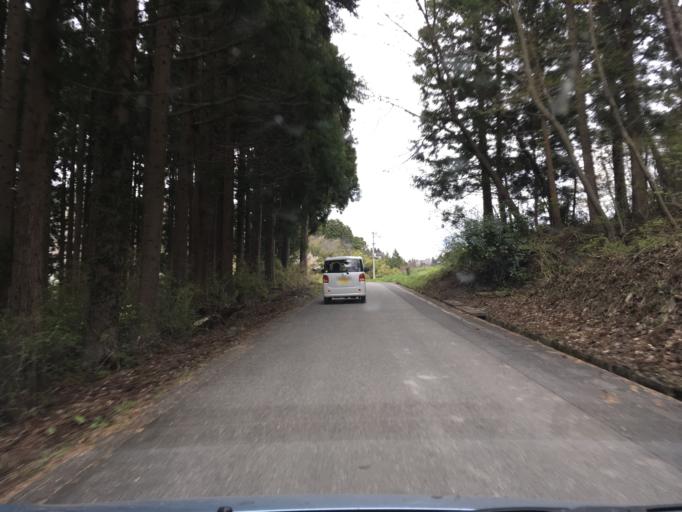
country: JP
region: Iwate
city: Ichinoseki
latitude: 38.9654
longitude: 141.1840
